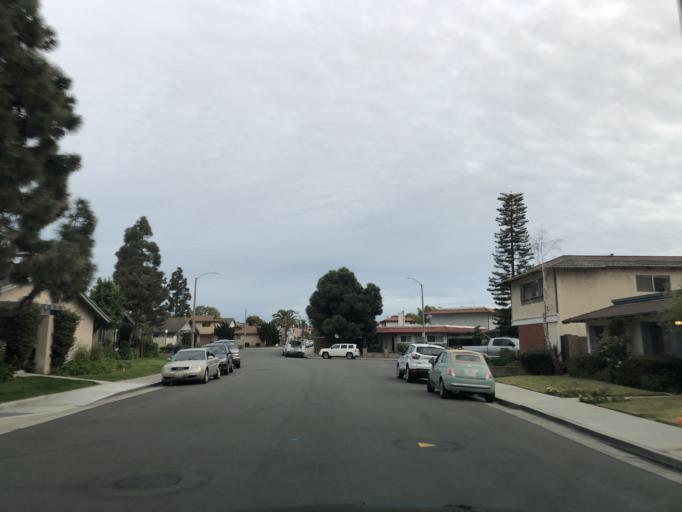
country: US
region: California
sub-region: Orange County
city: Westminster
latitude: 33.7217
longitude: -118.0481
